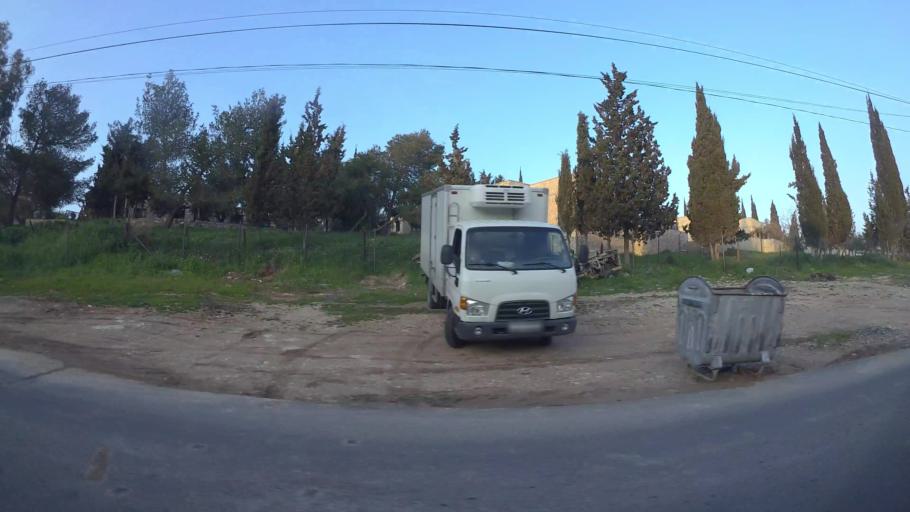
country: JO
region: Amman
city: Amman
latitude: 31.9935
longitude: 35.9540
